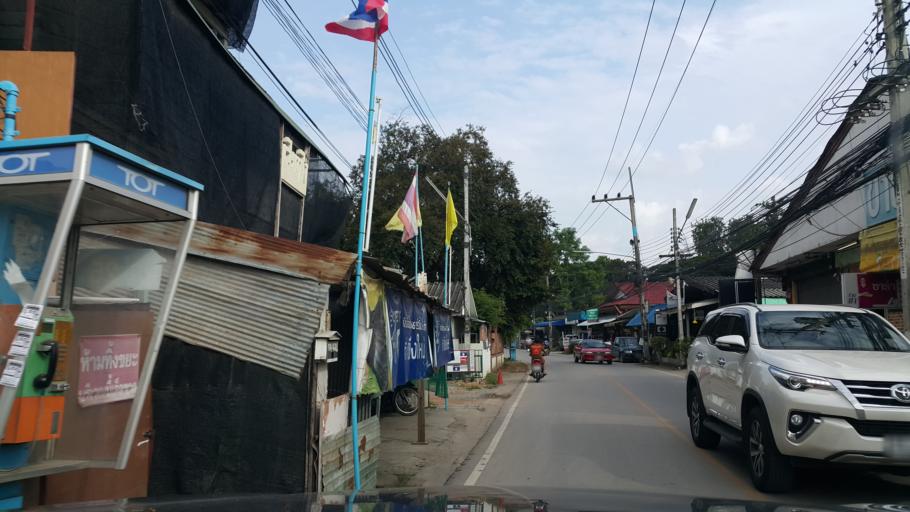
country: TH
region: Chiang Mai
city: Chiang Mai
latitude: 18.7902
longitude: 99.0273
